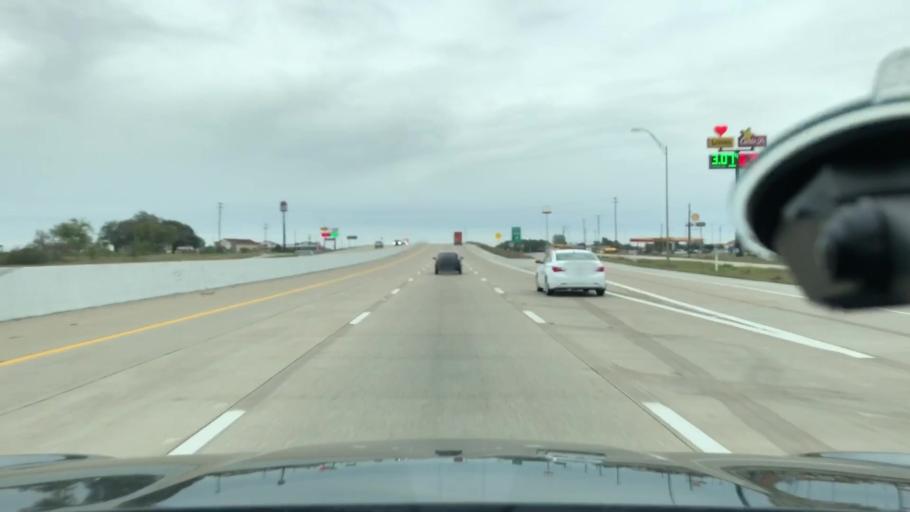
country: US
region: Texas
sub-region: Ellis County
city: Italy
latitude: 32.1919
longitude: -96.9012
